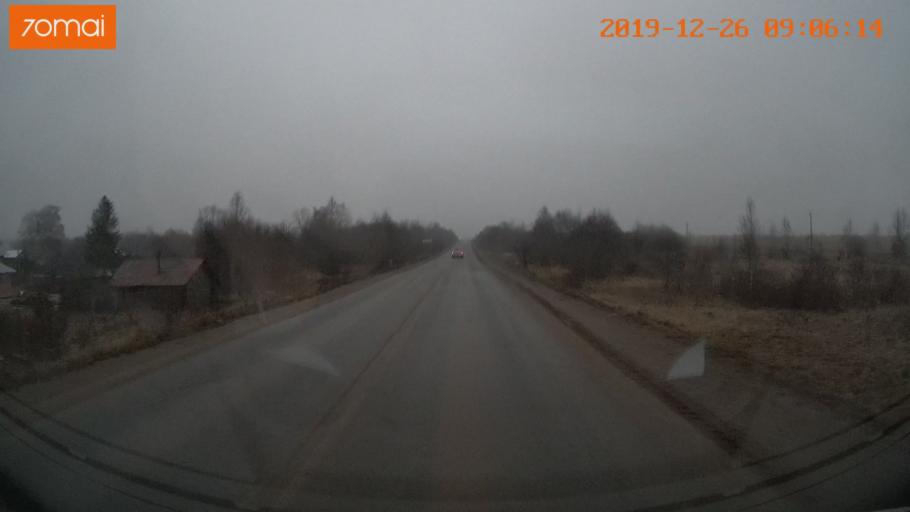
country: RU
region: Vologda
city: Gryazovets
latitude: 58.8339
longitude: 40.2542
